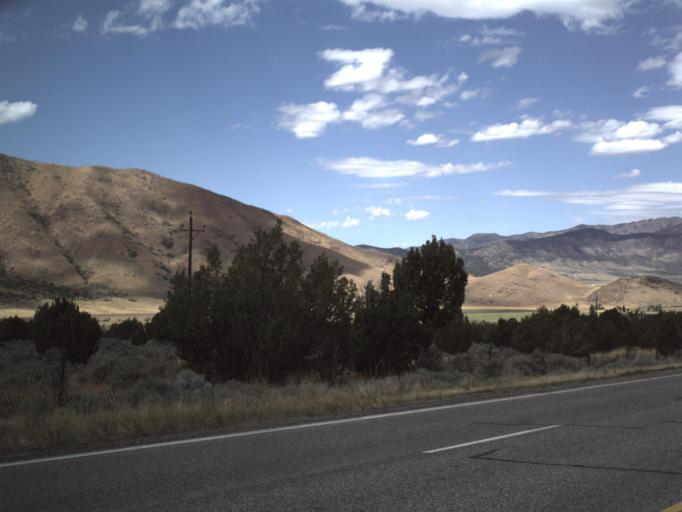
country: US
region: Utah
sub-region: Sanpete County
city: Gunnison
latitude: 39.1977
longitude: -112.0828
